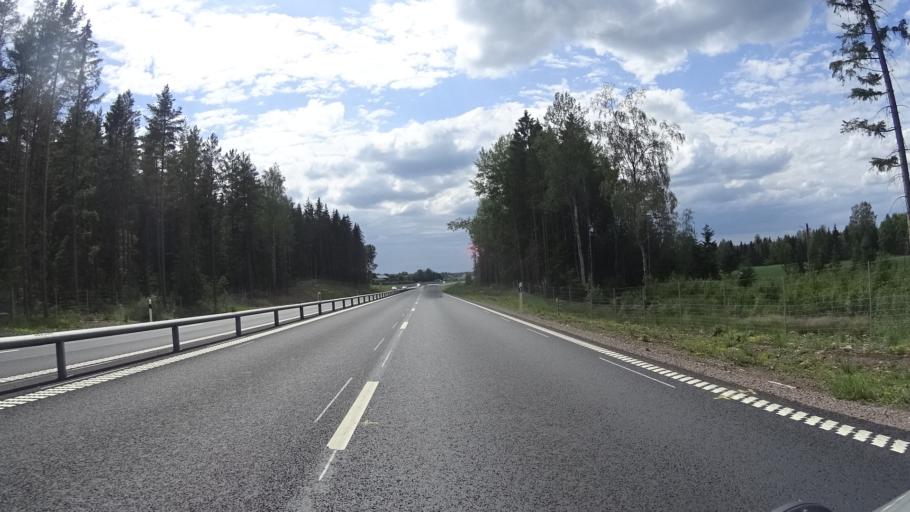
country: SE
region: Vaestra Goetaland
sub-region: Gullspangs Kommun
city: Hova
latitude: 58.8308
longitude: 14.1745
